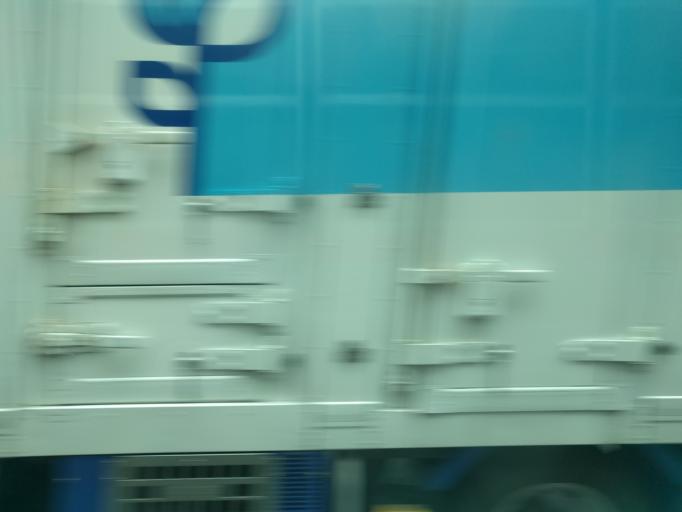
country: JP
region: Tokyo
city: Tokyo
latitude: 35.6313
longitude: 139.7091
